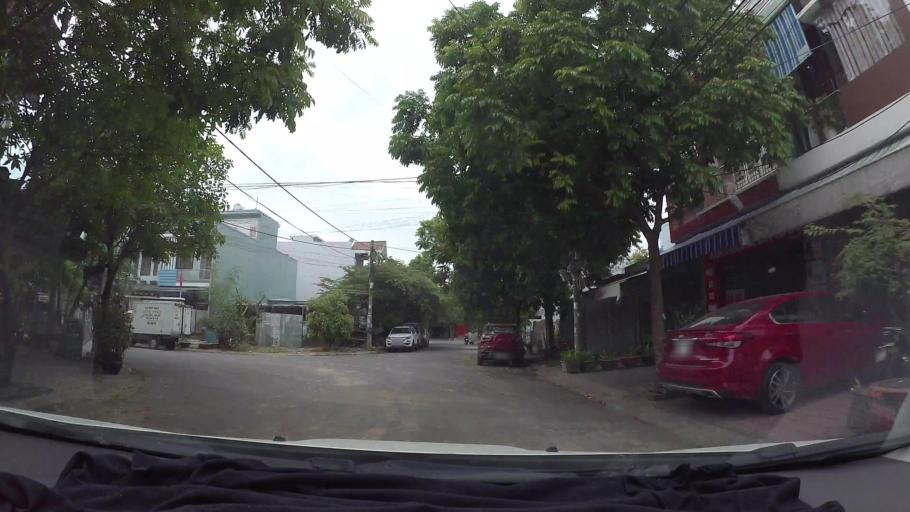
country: VN
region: Da Nang
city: Lien Chieu
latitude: 16.0580
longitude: 108.1698
